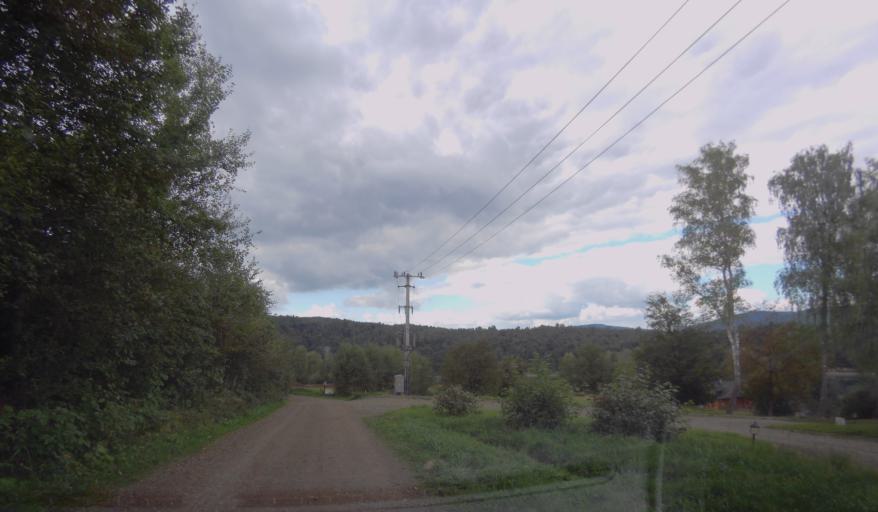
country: PL
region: Subcarpathian Voivodeship
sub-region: Powiat leski
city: Polanczyk
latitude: 49.3185
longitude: 22.5056
